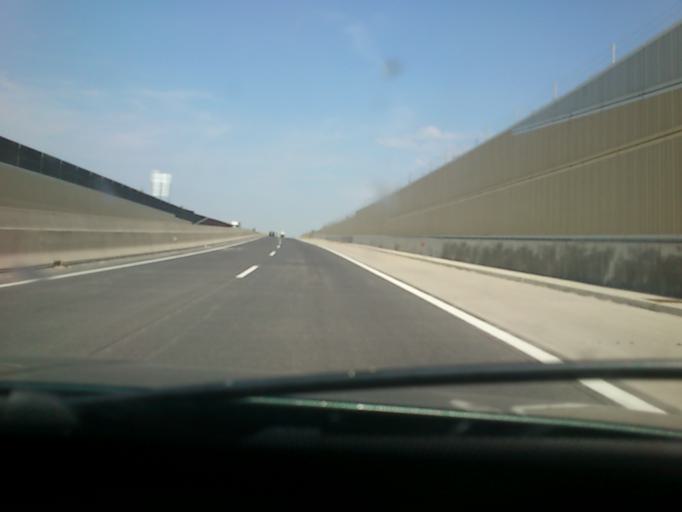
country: AT
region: Lower Austria
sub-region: Politischer Bezirk Ganserndorf
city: Aderklaa
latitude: 48.2920
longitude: 16.5136
